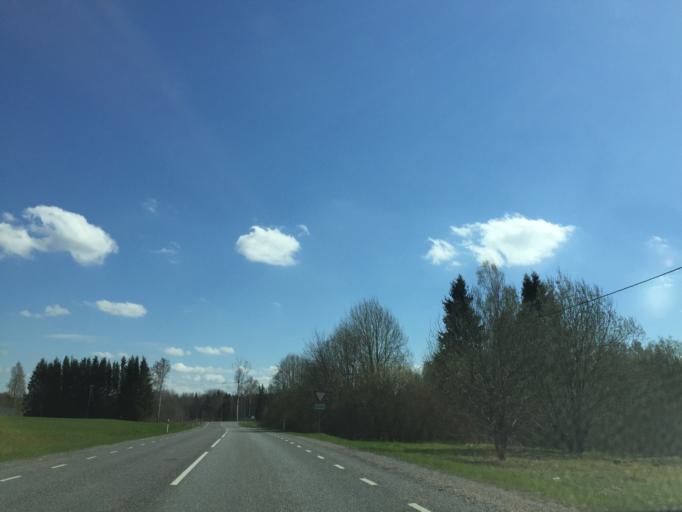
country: EE
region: Tartu
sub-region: Elva linn
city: Elva
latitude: 58.1480
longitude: 26.2288
